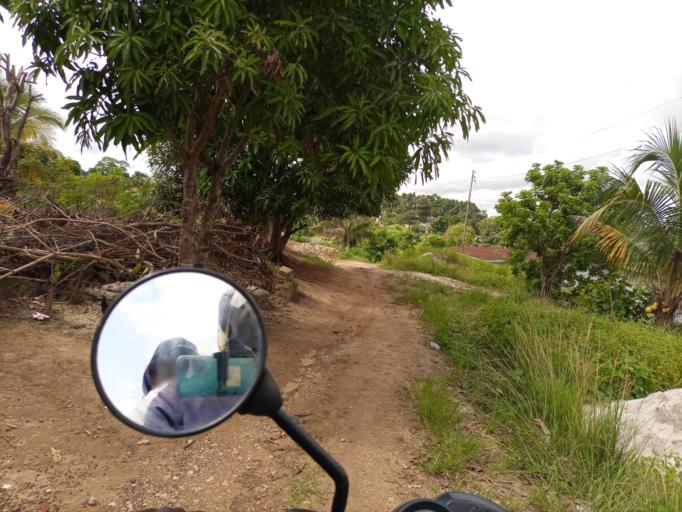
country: SL
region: Southern Province
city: Bo
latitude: 7.9720
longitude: -11.7567
